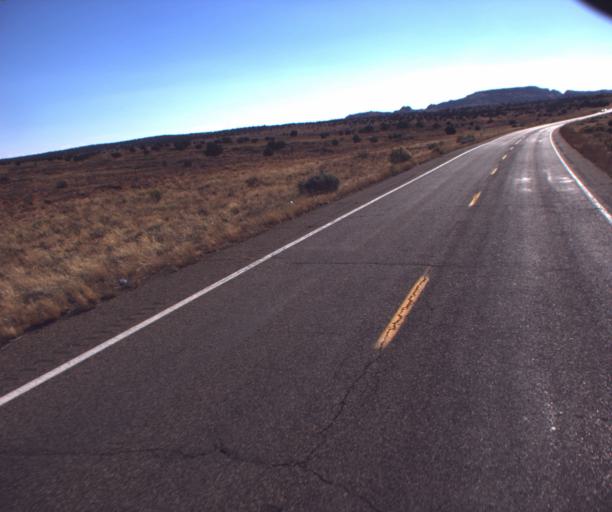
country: US
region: Arizona
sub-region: Coconino County
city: Kaibito
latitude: 36.5845
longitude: -111.1055
